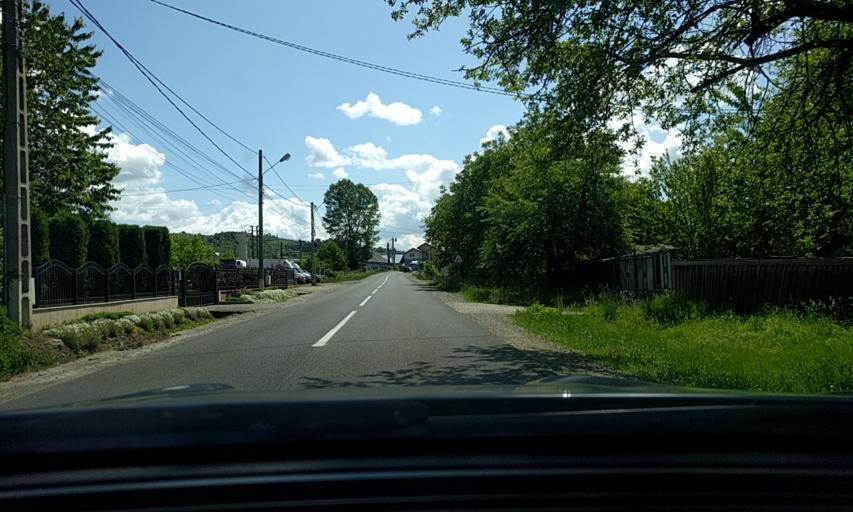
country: RO
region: Bistrita-Nasaud
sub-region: Oras Nasaud
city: Nasaud
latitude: 47.2974
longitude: 24.3781
